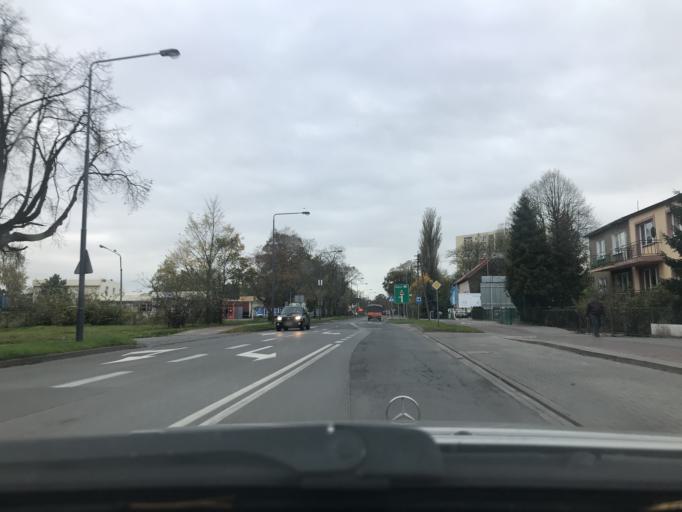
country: PL
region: West Pomeranian Voivodeship
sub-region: Swinoujscie
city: Swinoujscie
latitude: 53.9021
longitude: 14.2370
